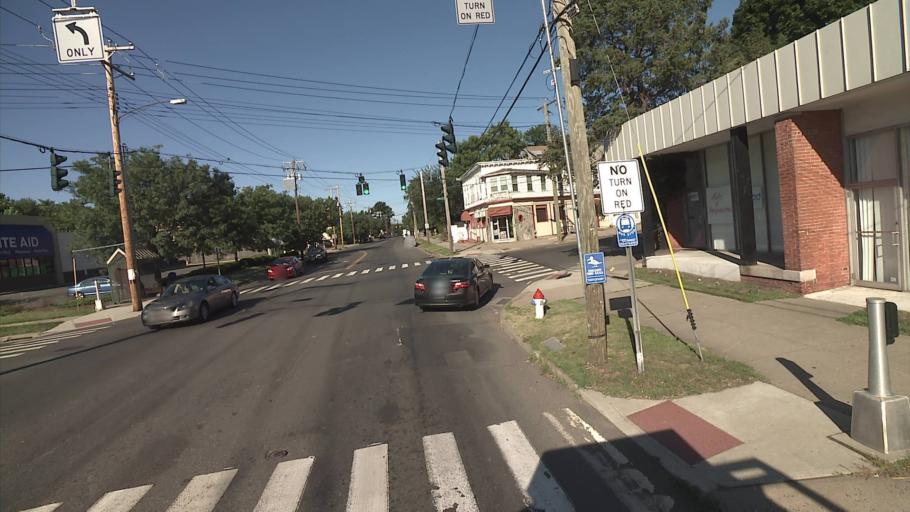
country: US
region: Connecticut
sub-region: New Haven County
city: West Haven
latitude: 41.2792
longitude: -72.9418
